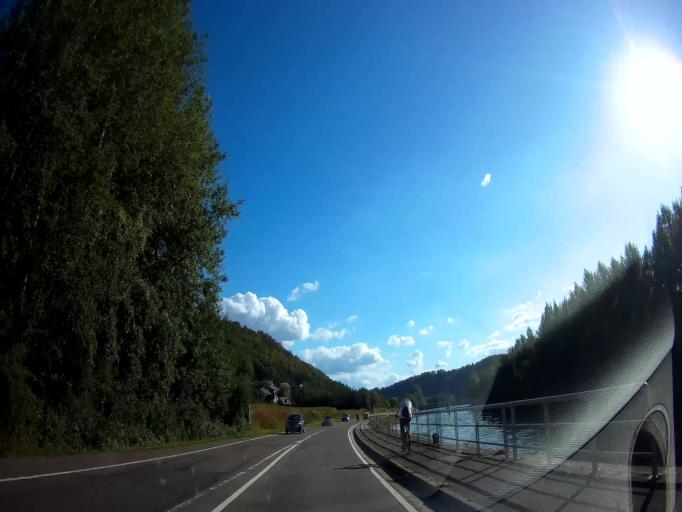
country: BE
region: Wallonia
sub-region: Province de Namur
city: Anhee
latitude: 50.2986
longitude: 4.8993
